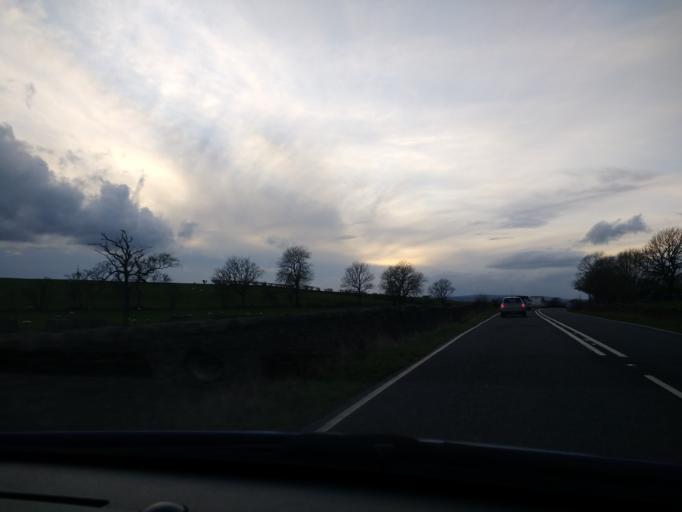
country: GB
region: England
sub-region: North Yorkshire
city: Ingleton
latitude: 54.1296
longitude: -2.4478
